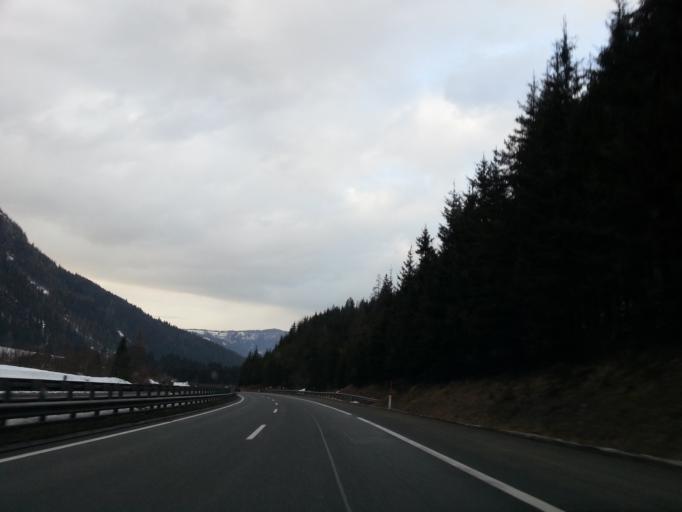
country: AT
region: Salzburg
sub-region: Politischer Bezirk Sankt Johann im Pongau
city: Flachau
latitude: 47.3154
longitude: 13.3968
